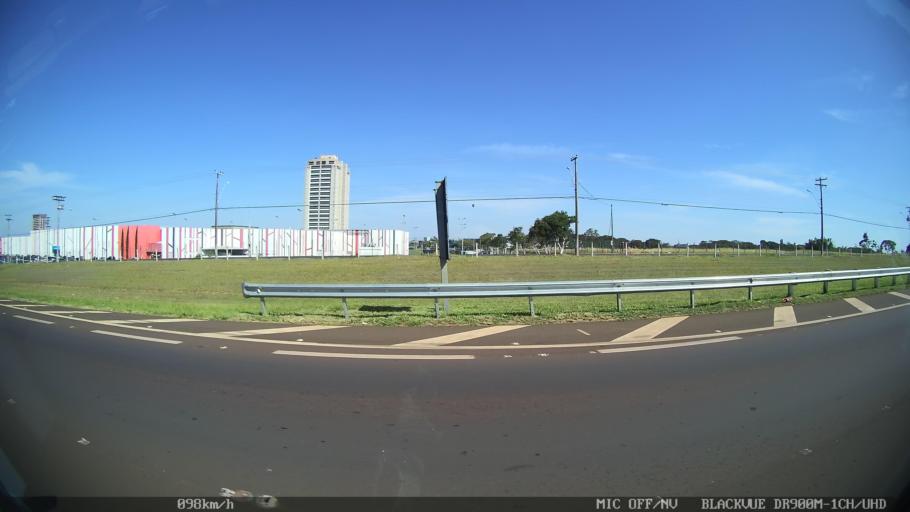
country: BR
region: Sao Paulo
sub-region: Franca
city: Franca
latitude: -20.5453
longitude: -47.4169
